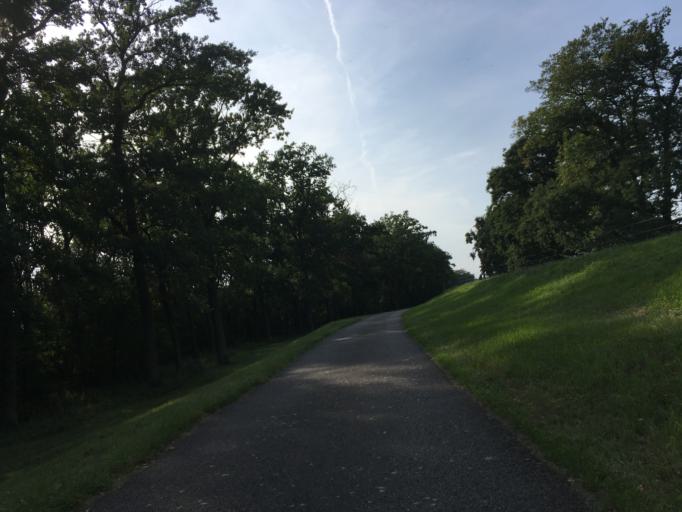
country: DE
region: Brandenburg
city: Brieskow-Finkenheerd
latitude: 52.2694
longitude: 14.6093
